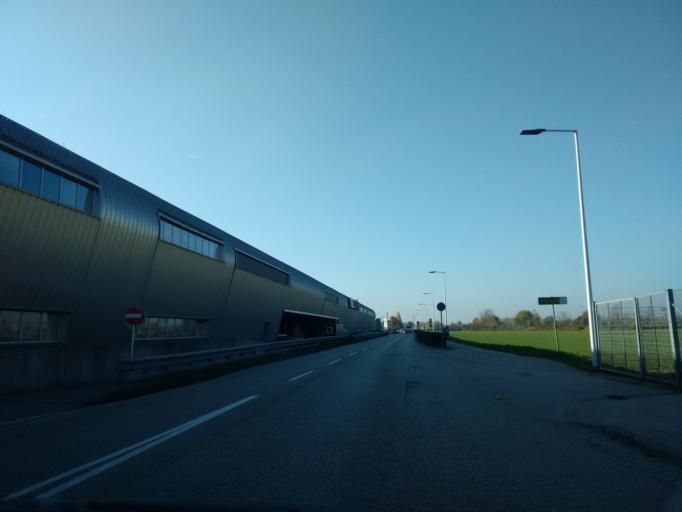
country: AT
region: Upper Austria
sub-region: Wels-Land
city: Gunskirchen
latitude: 48.1468
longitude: 13.9726
